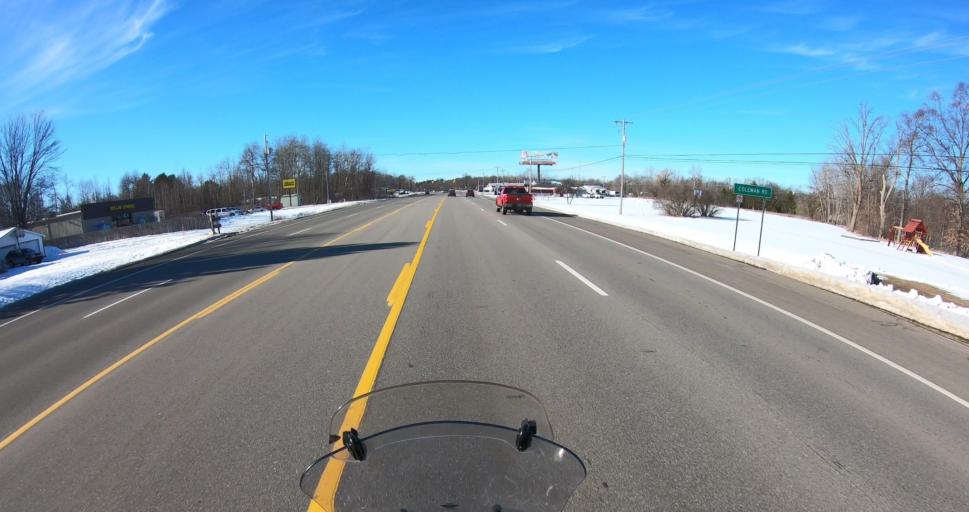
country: US
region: Michigan
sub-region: Isabella County
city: Shepherd
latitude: 43.6094
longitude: -84.5845
